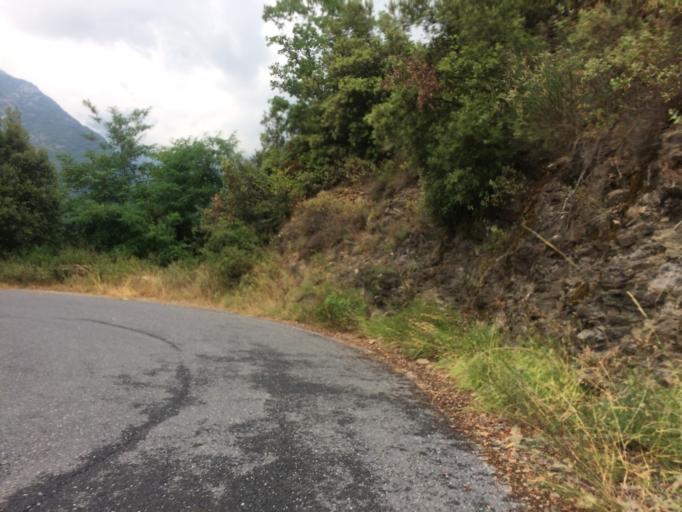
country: IT
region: Liguria
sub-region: Provincia di Imperia
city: Castel Vittorio
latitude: 43.9481
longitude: 7.6894
